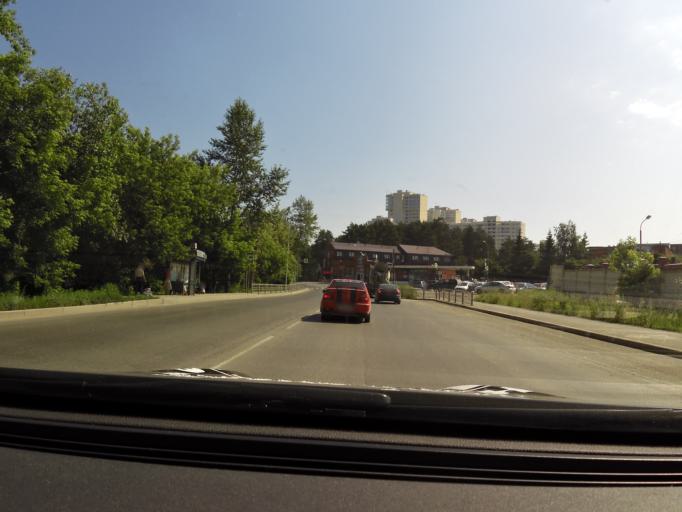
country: RU
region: Sverdlovsk
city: Shirokaya Rechka
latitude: 56.8100
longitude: 60.5064
